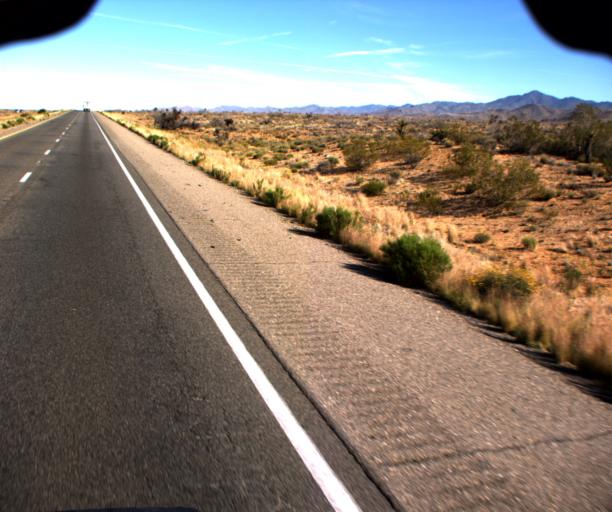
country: US
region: Arizona
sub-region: Mohave County
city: Golden Valley
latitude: 35.2664
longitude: -114.1646
